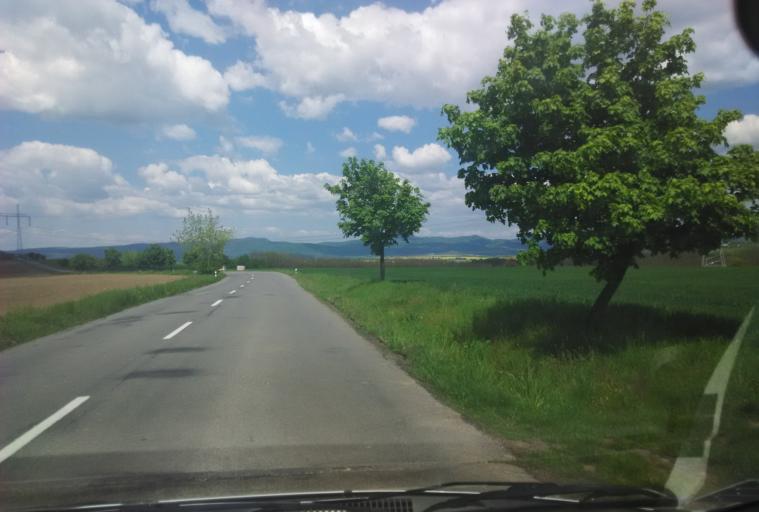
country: SK
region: Nitriansky
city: Levice
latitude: 48.2425
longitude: 18.7476
